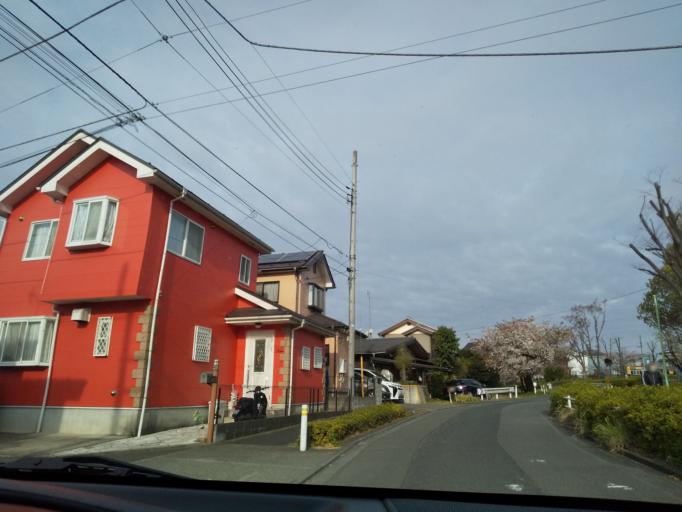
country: JP
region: Tokyo
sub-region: Machida-shi
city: Machida
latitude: 35.5926
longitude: 139.3909
